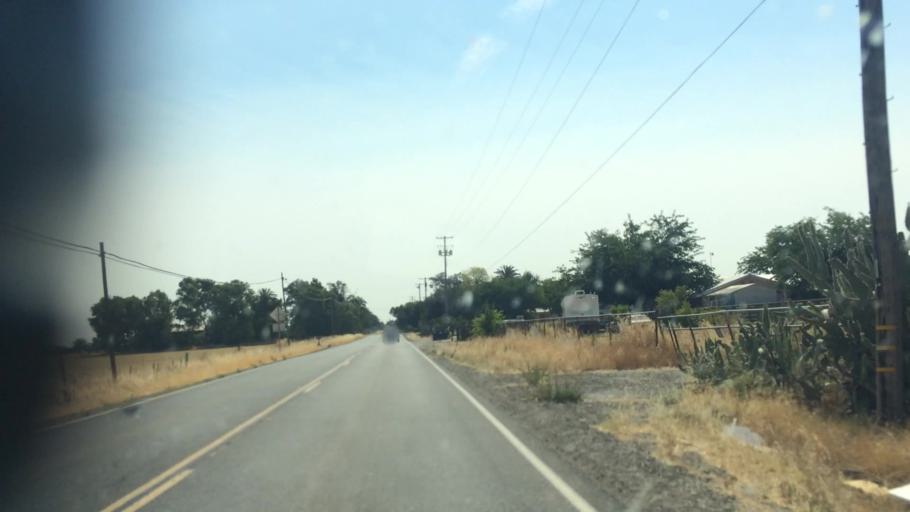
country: US
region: California
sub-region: Sacramento County
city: Herald
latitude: 38.2914
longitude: -121.2761
